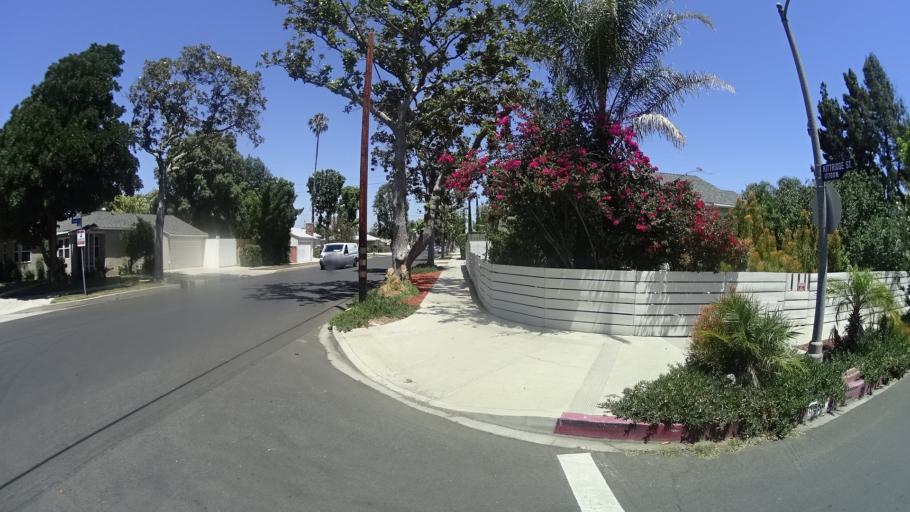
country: US
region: California
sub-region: Los Angeles County
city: Northridge
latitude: 34.1902
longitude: -118.5206
